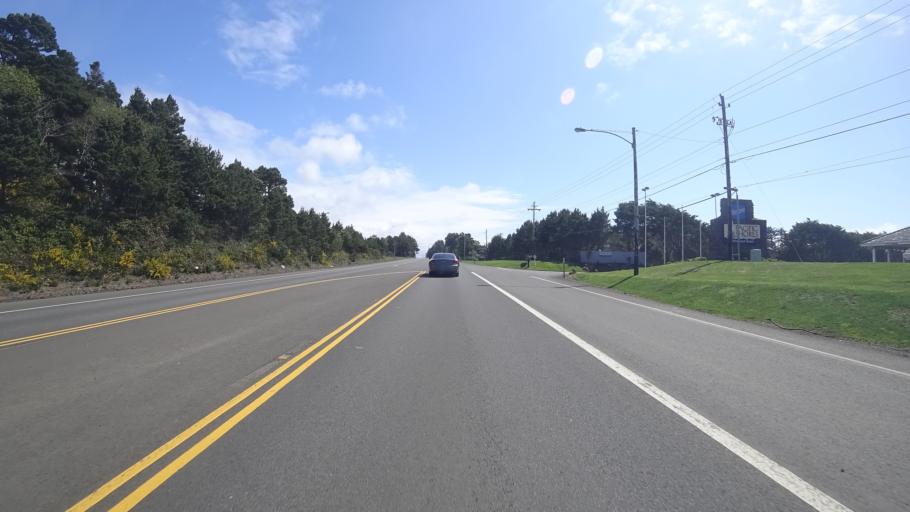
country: US
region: Oregon
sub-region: Lincoln County
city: Newport
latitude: 44.6825
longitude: -124.0632
